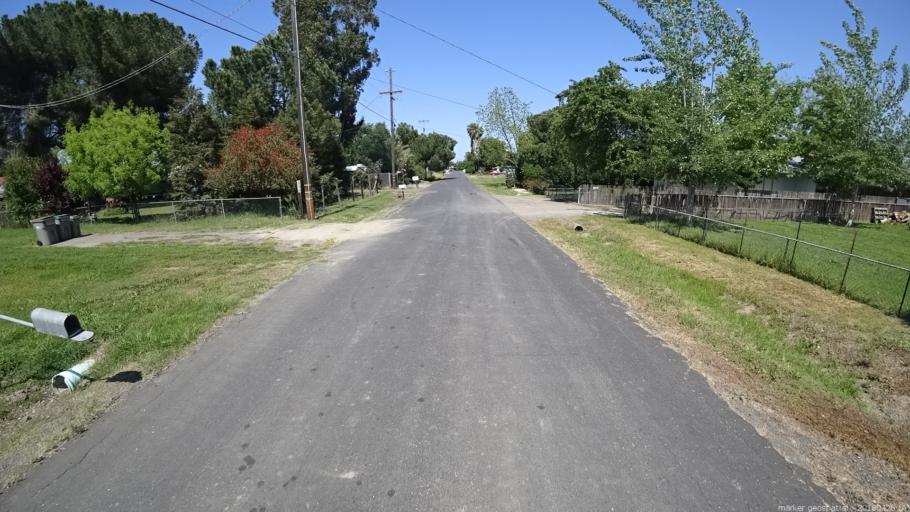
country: US
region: California
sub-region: Yolo County
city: West Sacramento
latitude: 38.5444
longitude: -121.5482
